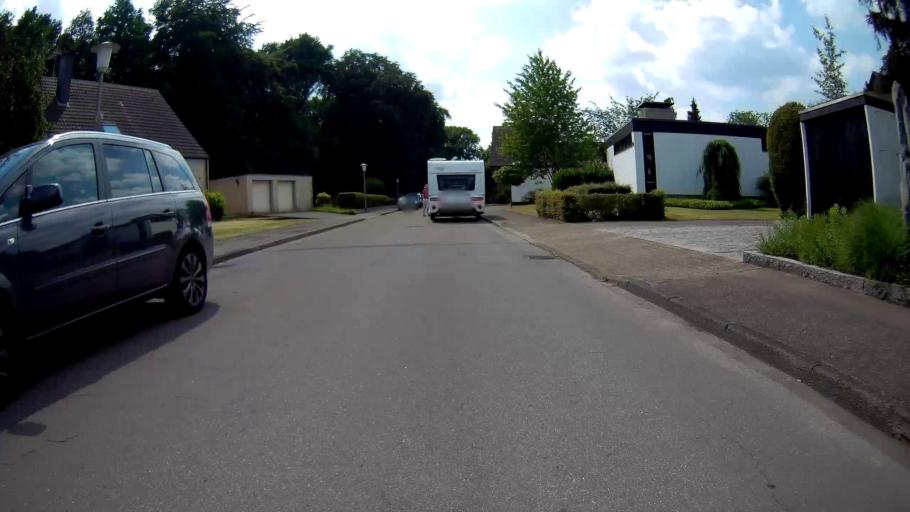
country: DE
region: North Rhine-Westphalia
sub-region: Regierungsbezirk Munster
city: Gladbeck
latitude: 51.5903
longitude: 6.9917
